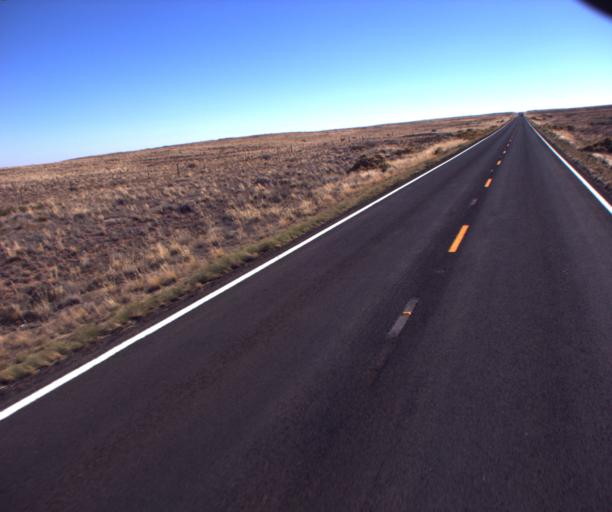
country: US
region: Arizona
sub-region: Coconino County
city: Tuba City
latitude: 35.9783
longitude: -110.9822
